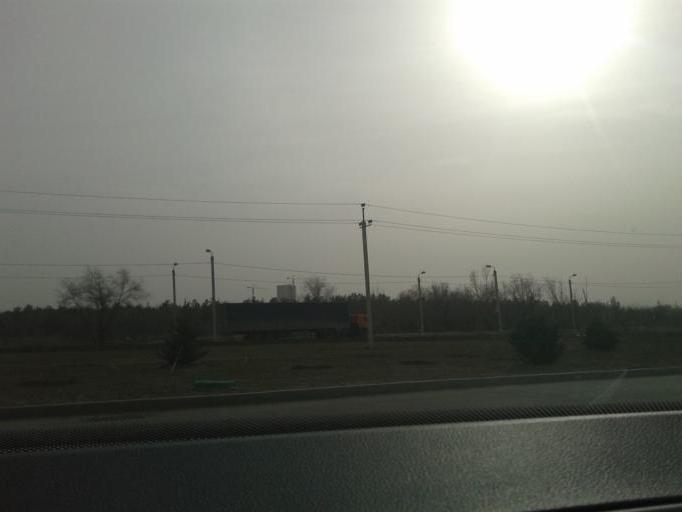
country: RU
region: Volgograd
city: Volgograd
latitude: 48.6340
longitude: 44.4341
